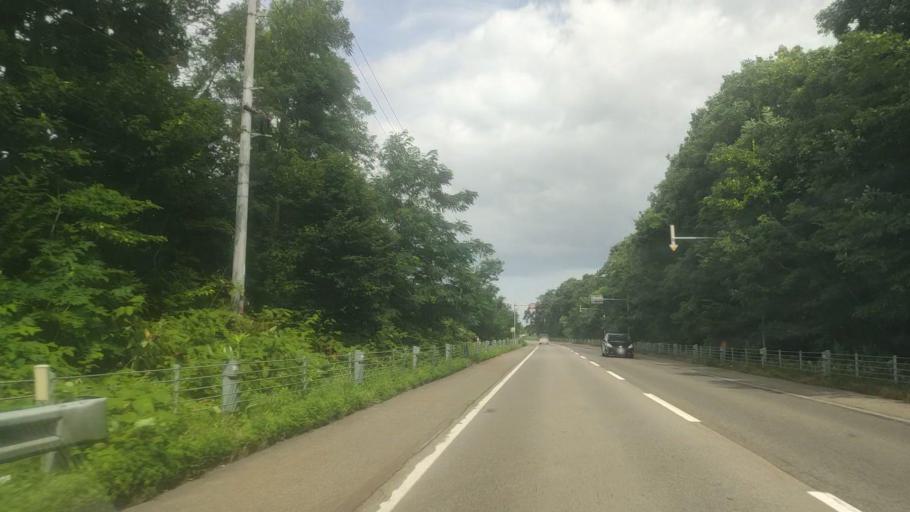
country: JP
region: Hokkaido
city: Nanae
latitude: 42.0526
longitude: 140.5991
